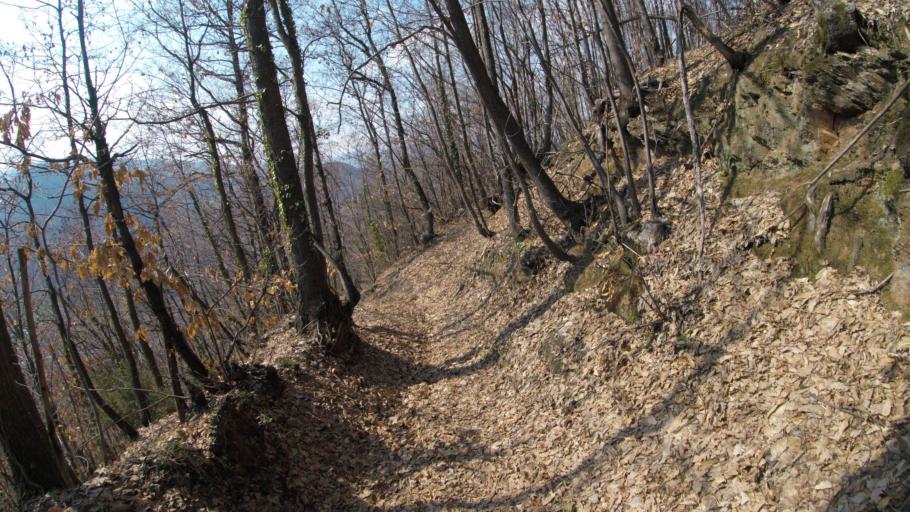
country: IT
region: Piedmont
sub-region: Provincia di Cuneo
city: Rossana
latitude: 44.5394
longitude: 7.4389
